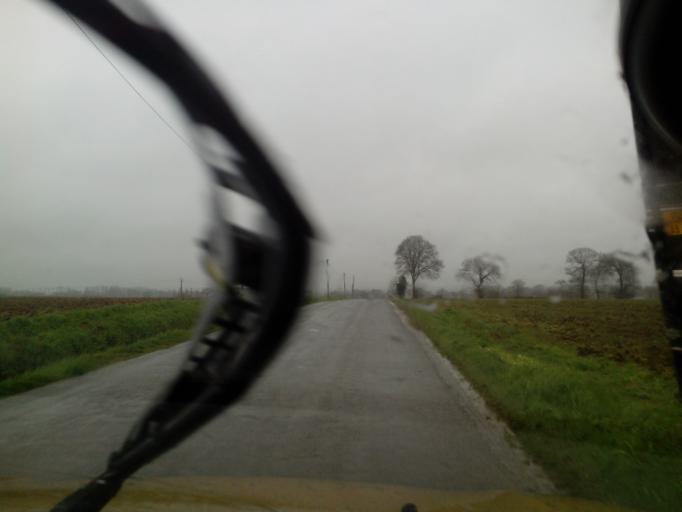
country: FR
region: Brittany
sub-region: Departement d'Ille-et-Vilaine
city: Melesse
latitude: 48.2092
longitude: -1.6640
